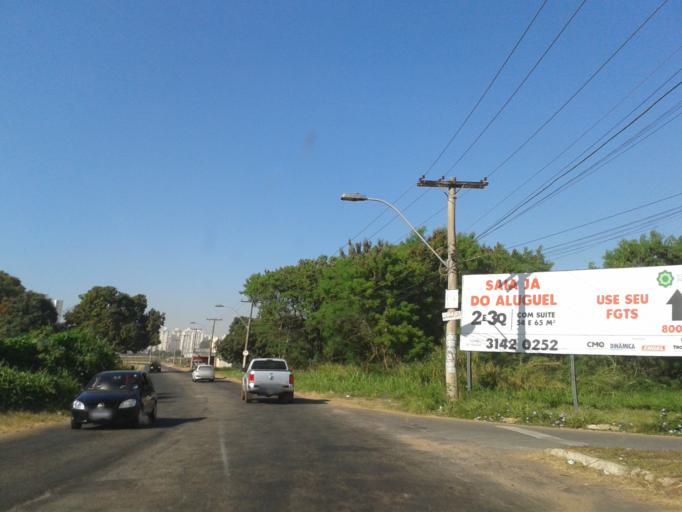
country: BR
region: Goias
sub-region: Goiania
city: Goiania
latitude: -16.6885
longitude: -49.3287
